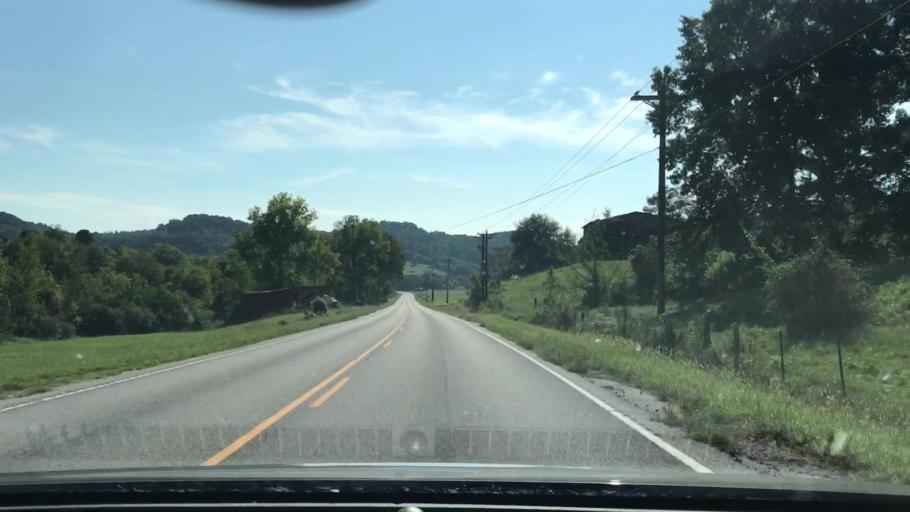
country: US
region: Tennessee
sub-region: Jackson County
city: Gainesboro
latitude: 36.3472
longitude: -85.8178
